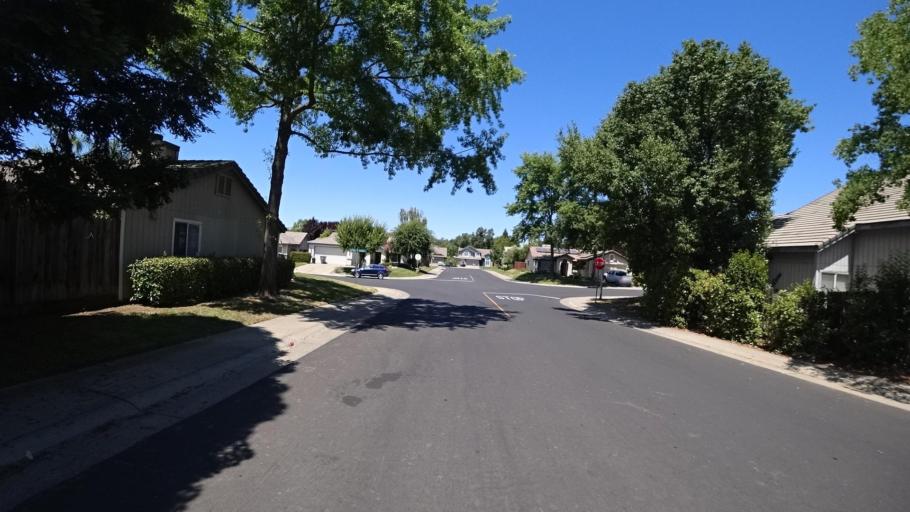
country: US
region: California
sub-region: Placer County
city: Rocklin
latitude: 38.8247
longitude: -121.2539
